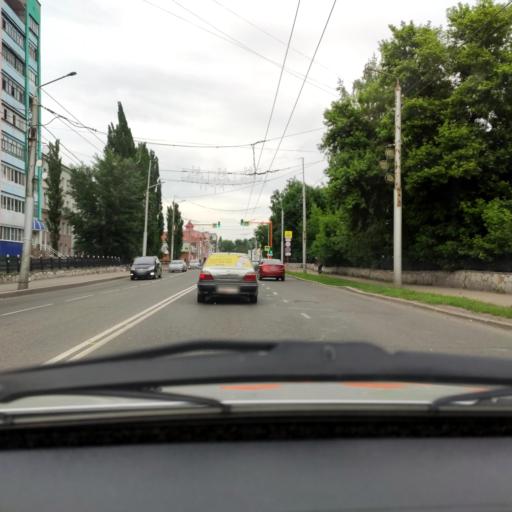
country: RU
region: Bashkortostan
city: Sterlitamak
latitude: 53.6174
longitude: 55.9591
